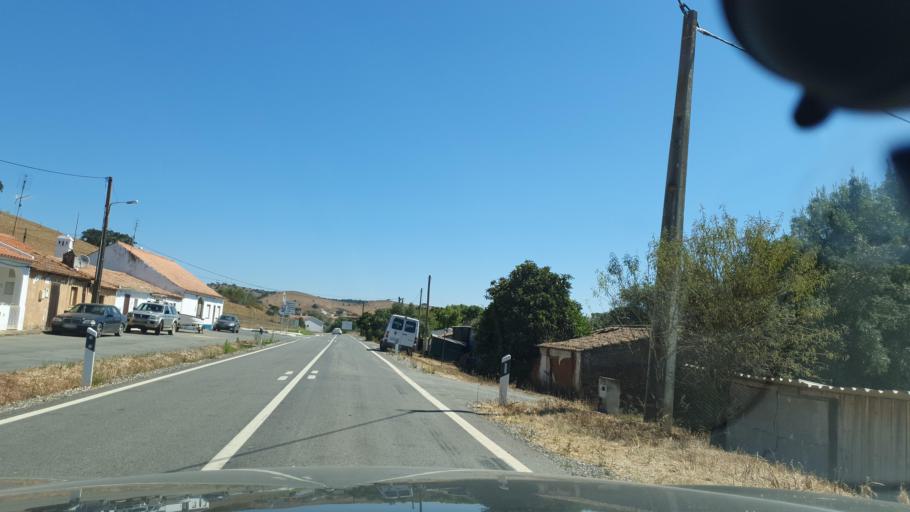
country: PT
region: Faro
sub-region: Monchique
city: Monchique
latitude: 37.4850
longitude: -8.4872
